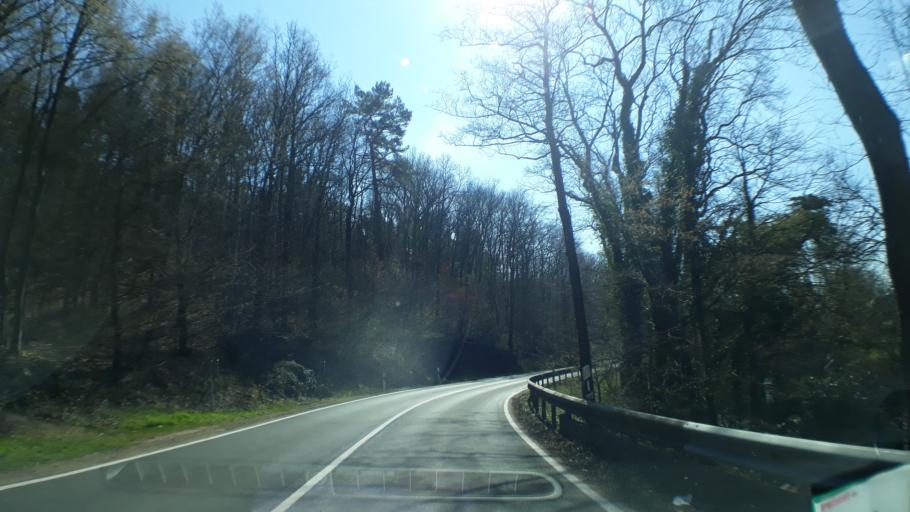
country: DE
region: North Rhine-Westphalia
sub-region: Regierungsbezirk Koln
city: Mechernich
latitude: 50.6031
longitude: 6.6866
